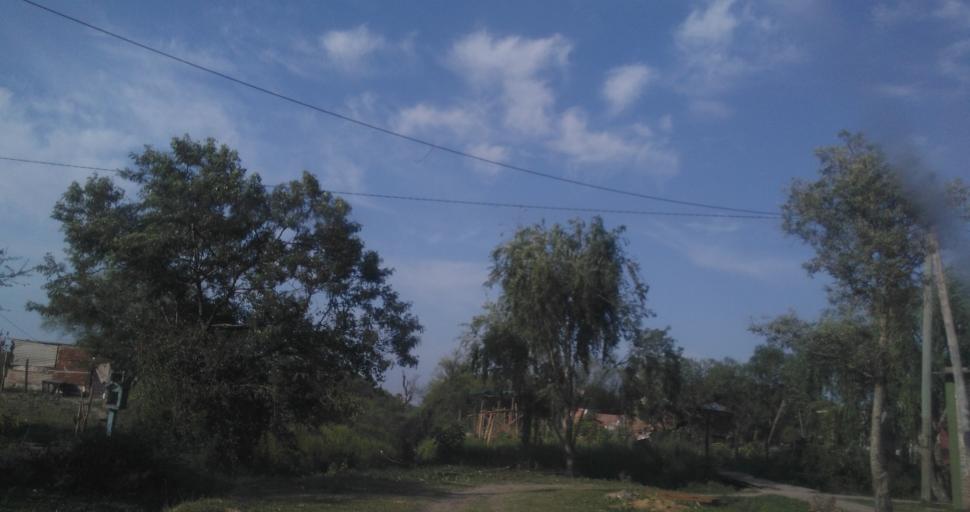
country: AR
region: Chaco
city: Resistencia
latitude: -27.4844
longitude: -59.0059
